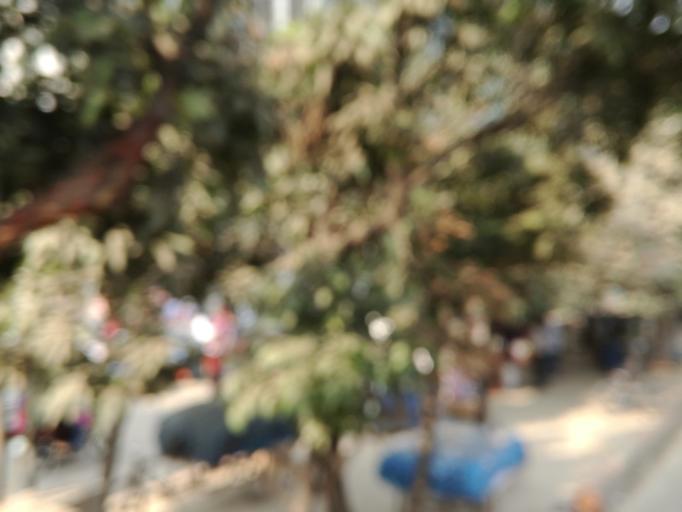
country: BD
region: Dhaka
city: Tungi
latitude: 23.8670
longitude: 90.4000
